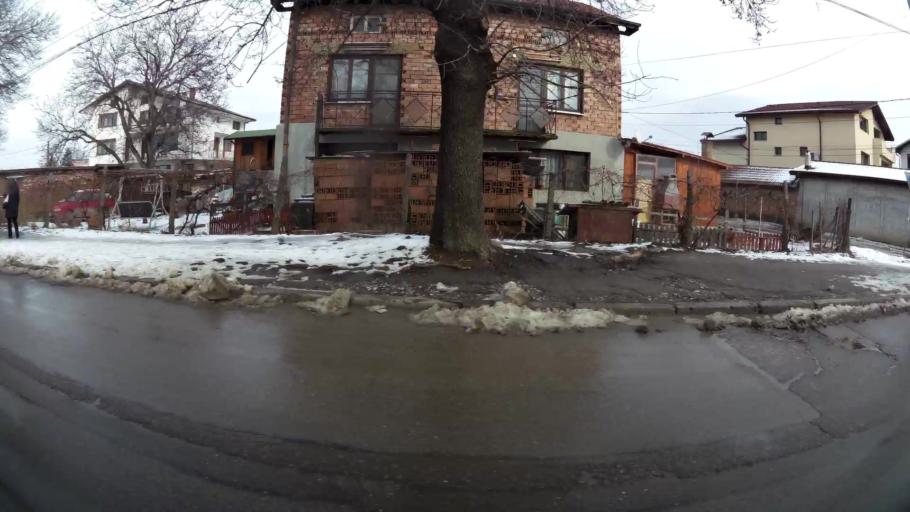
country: BG
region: Sofia-Capital
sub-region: Stolichna Obshtina
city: Sofia
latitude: 42.7130
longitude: 23.4188
